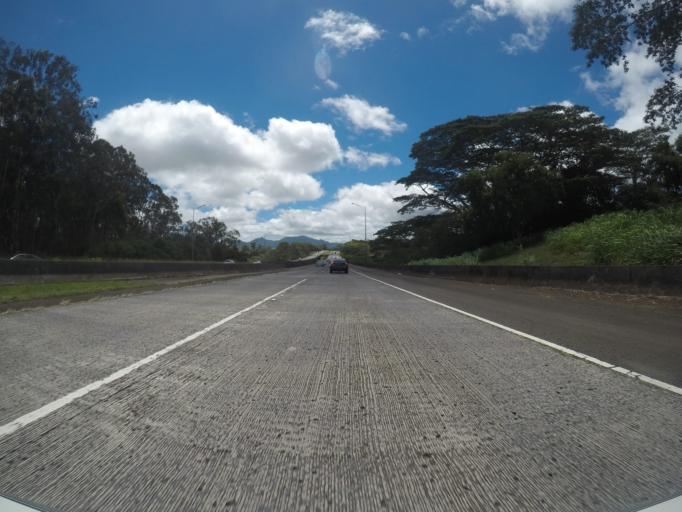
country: US
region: Hawaii
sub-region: Honolulu County
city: Waipi'o Acres
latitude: 21.4744
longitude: -158.0147
